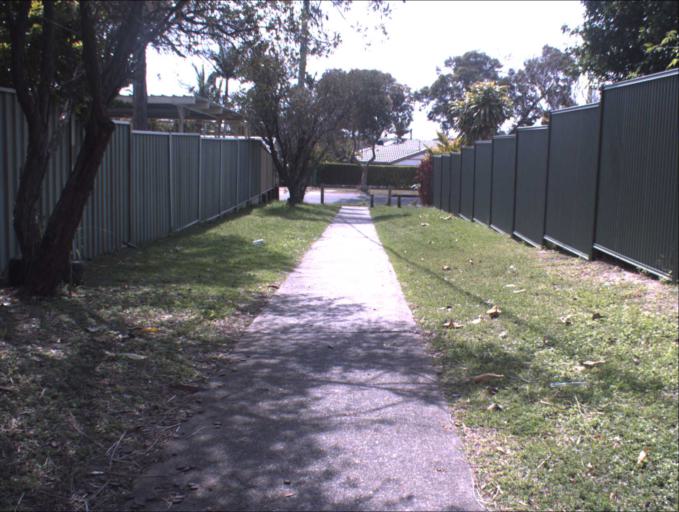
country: AU
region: Queensland
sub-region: Logan
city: Waterford West
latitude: -27.6813
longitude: 153.0963
